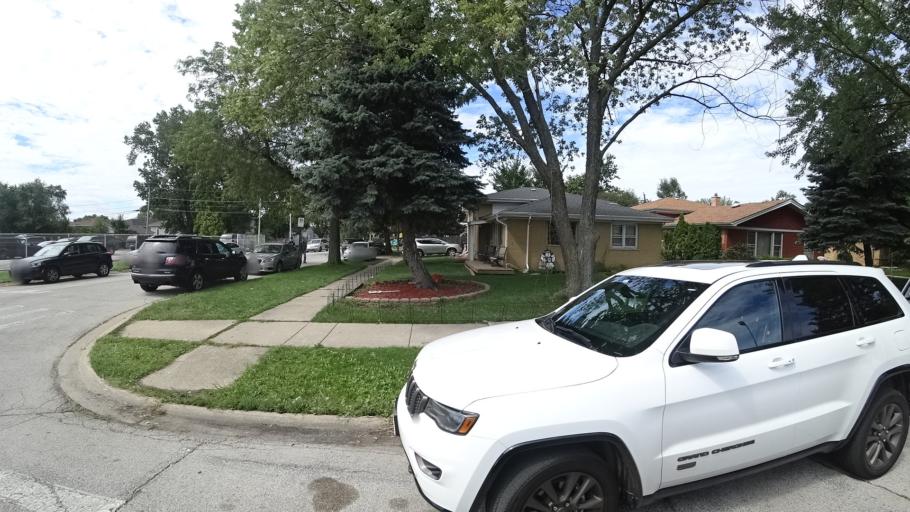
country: US
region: Illinois
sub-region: Cook County
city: Burbank
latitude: 41.7216
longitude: -87.7702
